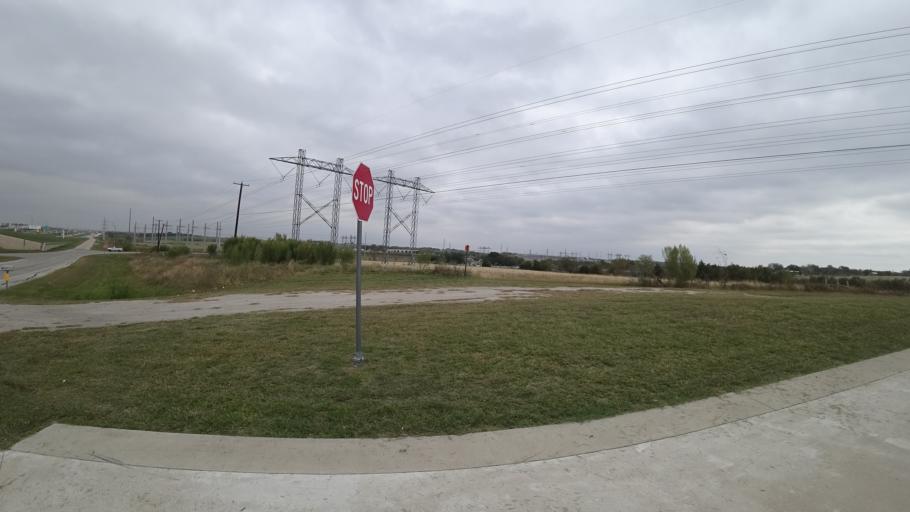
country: US
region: Texas
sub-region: Travis County
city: Pflugerville
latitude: 30.4052
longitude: -97.5823
